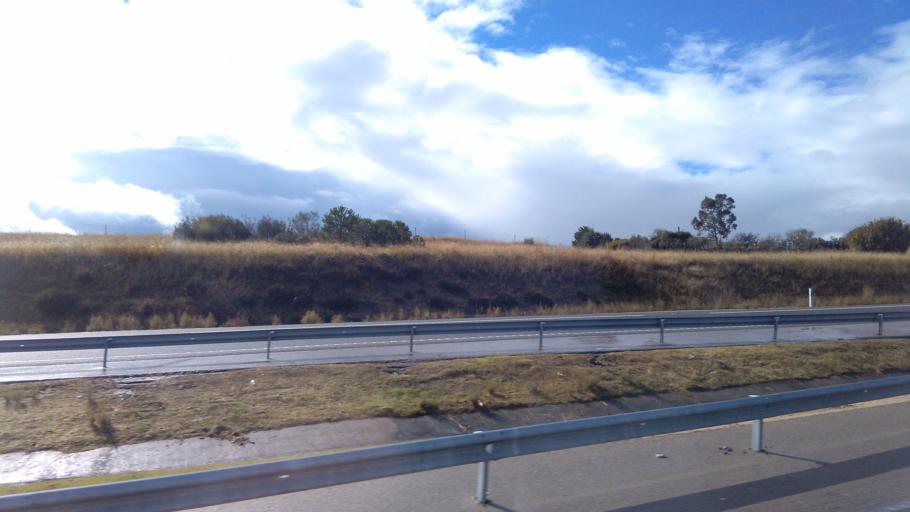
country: ES
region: Madrid
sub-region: Provincia de Madrid
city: Navalcarnero
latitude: 40.2655
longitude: -4.0225
